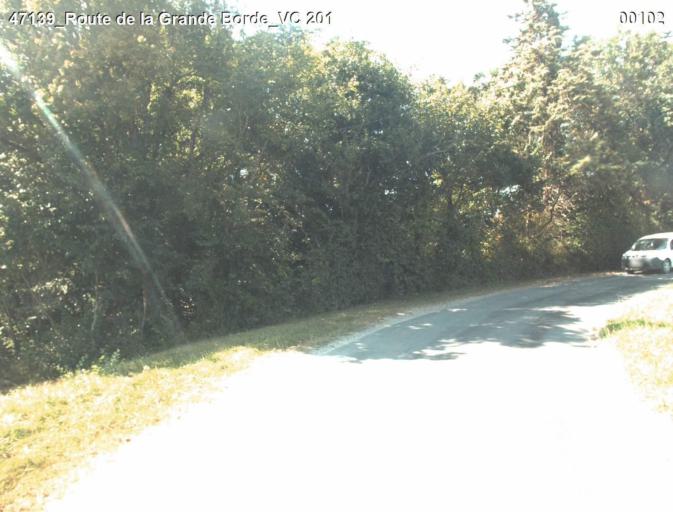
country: FR
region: Aquitaine
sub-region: Departement du Lot-et-Garonne
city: Nerac
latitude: 44.0633
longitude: 0.3933
